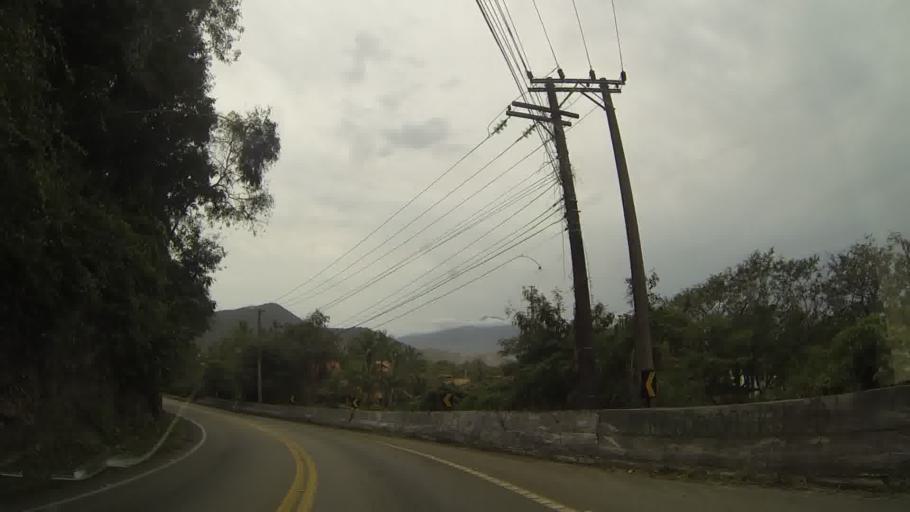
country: BR
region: Sao Paulo
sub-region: Sao Sebastiao
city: Sao Sebastiao
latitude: -23.8181
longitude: -45.4637
